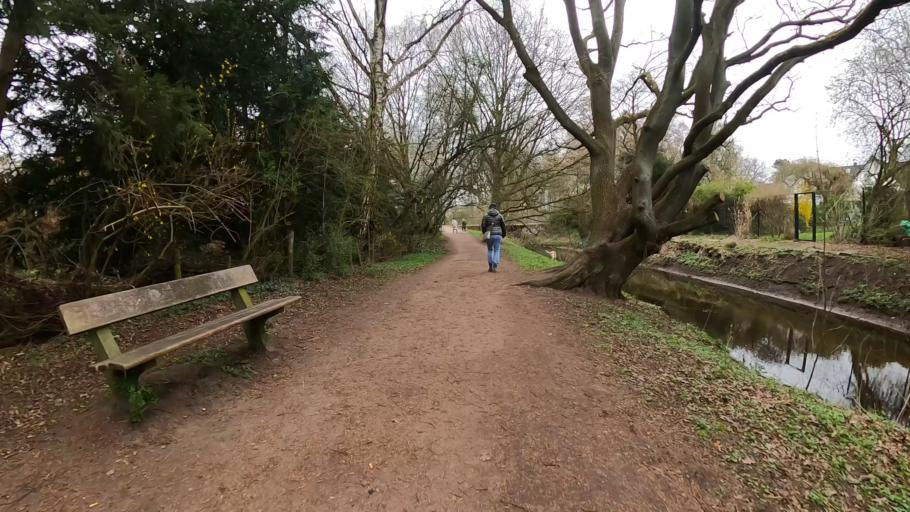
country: DE
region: Hamburg
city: Hamburg-Nord
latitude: 53.6092
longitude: 9.9649
